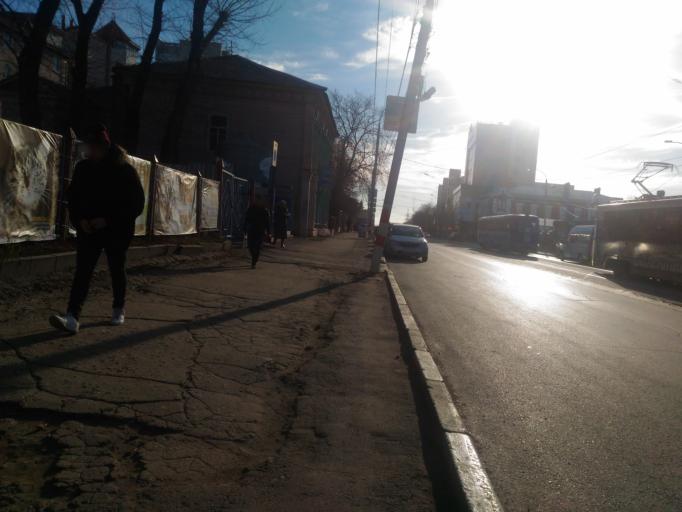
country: RU
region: Ulyanovsk
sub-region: Ulyanovskiy Rayon
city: Ulyanovsk
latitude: 54.3106
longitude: 48.3880
